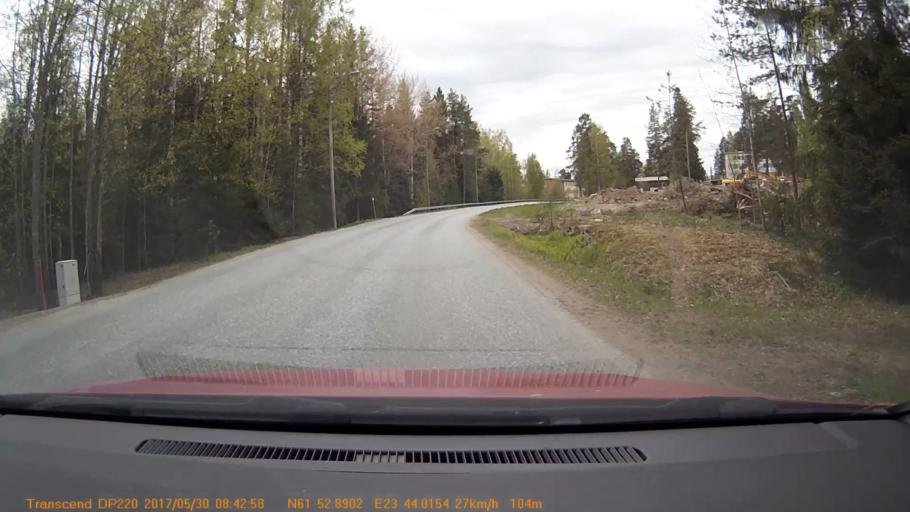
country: FI
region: Pirkanmaa
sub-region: Tampere
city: Kuru
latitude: 61.8815
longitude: 23.7336
